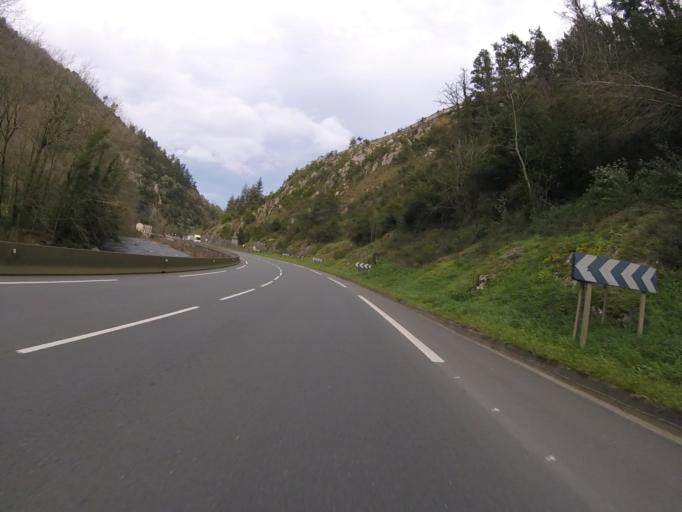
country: ES
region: Basque Country
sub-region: Provincia de Guipuzcoa
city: Cestona
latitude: 43.2442
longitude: -2.2584
